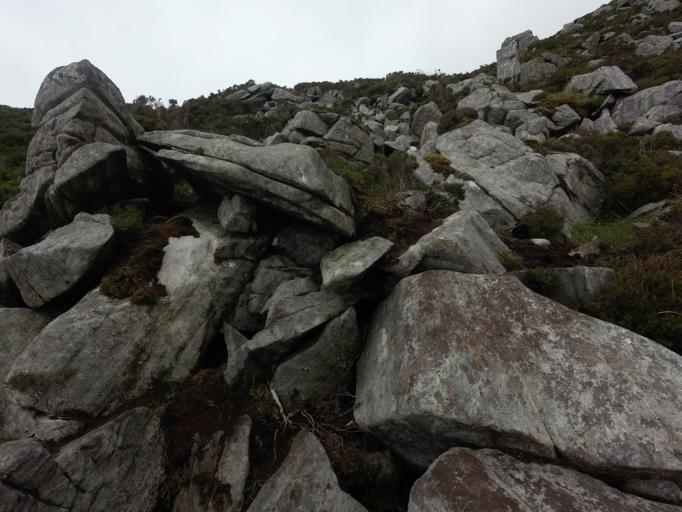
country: IE
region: Ulster
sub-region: County Donegal
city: Killybegs
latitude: 54.6435
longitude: -8.6866
